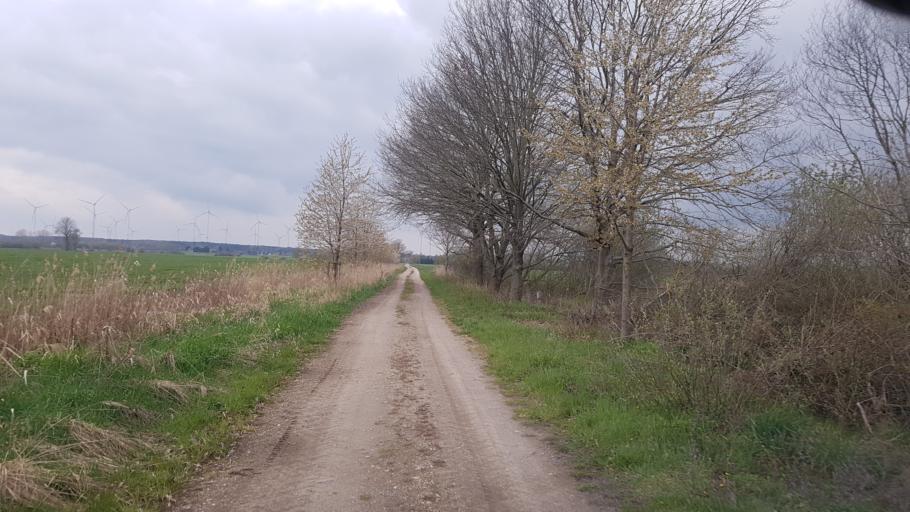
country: DE
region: Brandenburg
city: Bronkow
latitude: 51.6358
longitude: 13.8745
